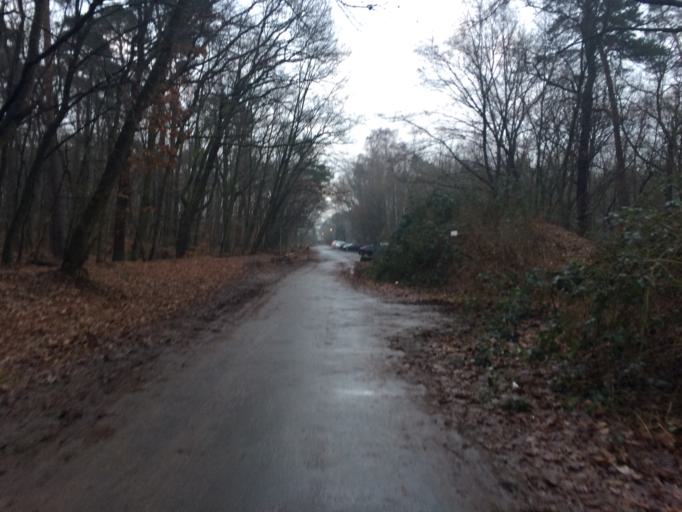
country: DE
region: Hesse
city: Morfelden-Walldorf
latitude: 50.0378
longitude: 8.6019
